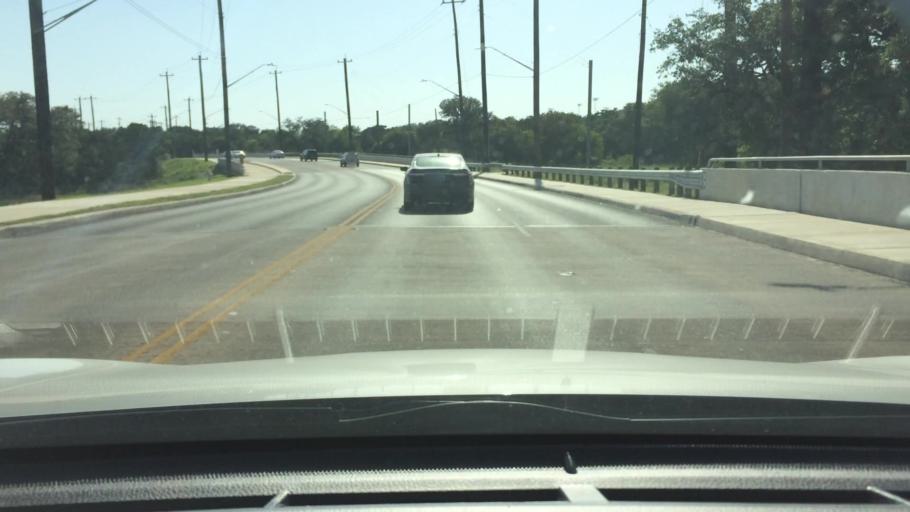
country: US
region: Texas
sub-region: Bexar County
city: Helotes
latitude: 29.5721
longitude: -98.6342
